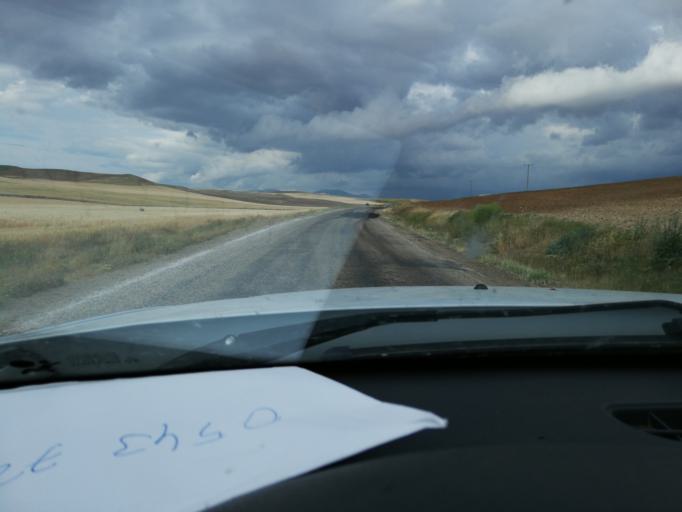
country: TR
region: Kirsehir
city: Kirsehir
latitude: 39.0397
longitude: 34.1497
